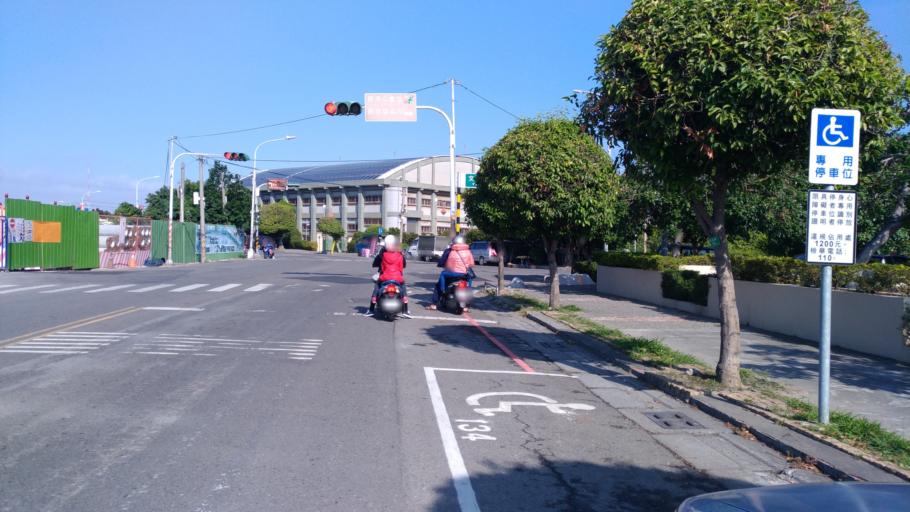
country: TW
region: Taiwan
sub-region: Changhua
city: Chang-hua
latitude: 24.0555
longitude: 120.4294
